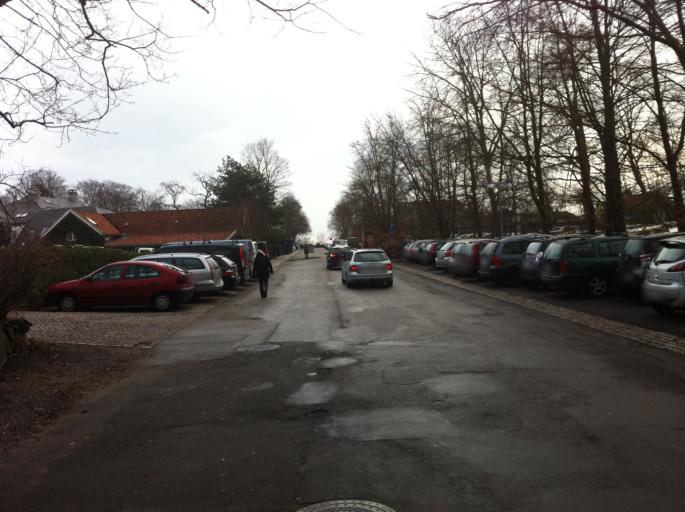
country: DK
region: Capital Region
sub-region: Fredensborg Kommune
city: Humlebaek
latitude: 55.9698
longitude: 12.5411
